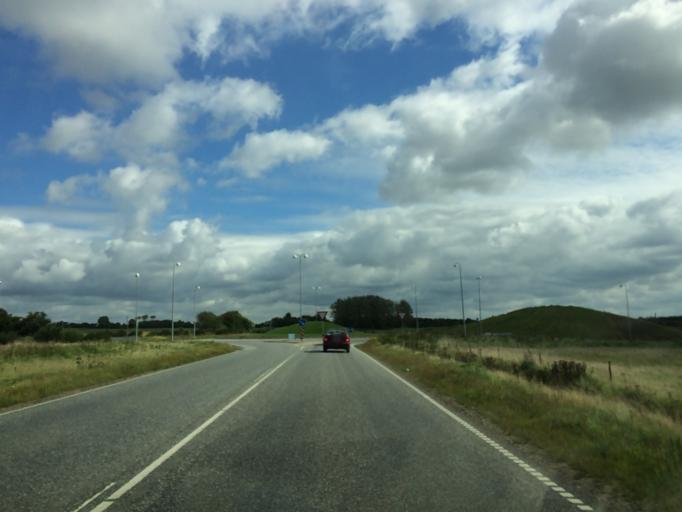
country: DK
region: Central Jutland
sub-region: Holstebro Kommune
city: Holstebro
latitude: 56.3631
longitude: 8.6741
